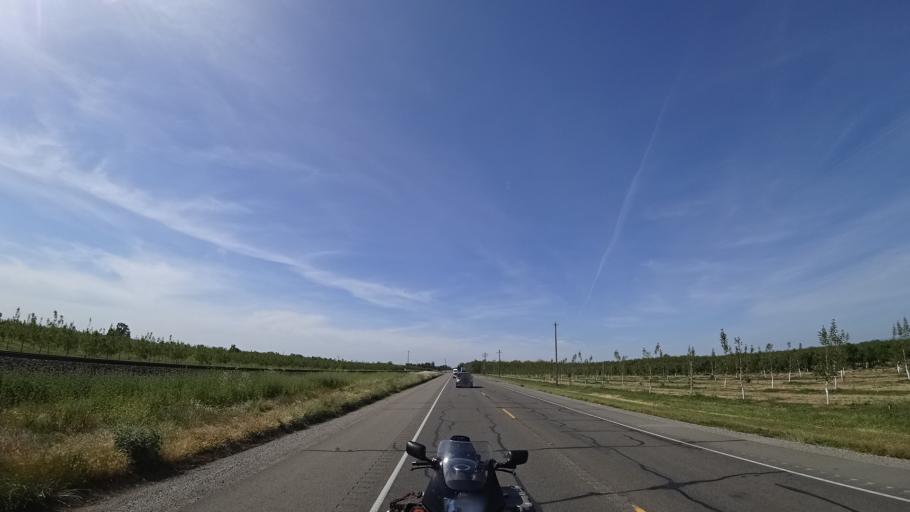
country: US
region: California
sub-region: Tehama County
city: Los Molinos
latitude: 40.0012
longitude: -122.0899
